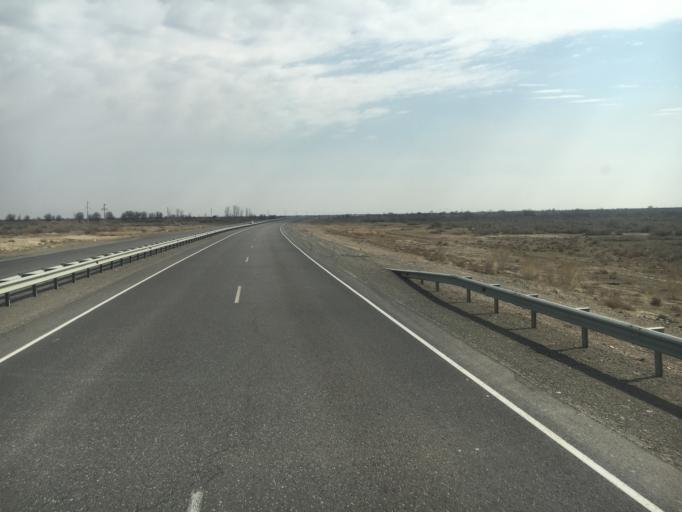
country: KZ
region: Qyzylorda
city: Belkol
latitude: 44.6701
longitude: 65.9813
